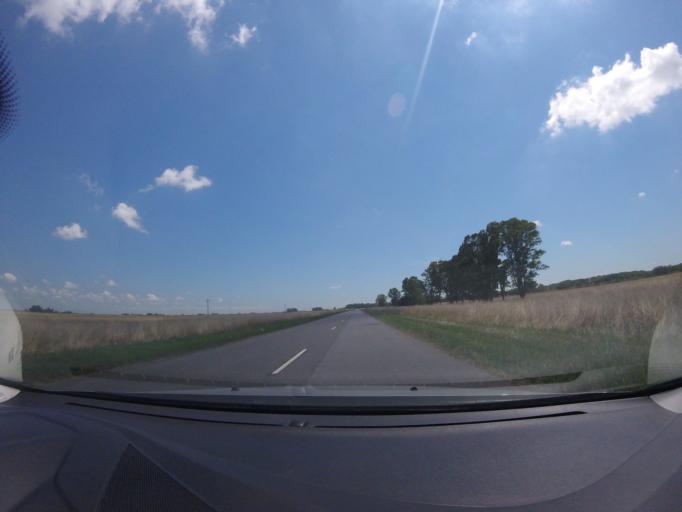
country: AR
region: Buenos Aires
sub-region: Partido de Rauch
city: Rauch
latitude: -36.6812
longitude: -59.0649
